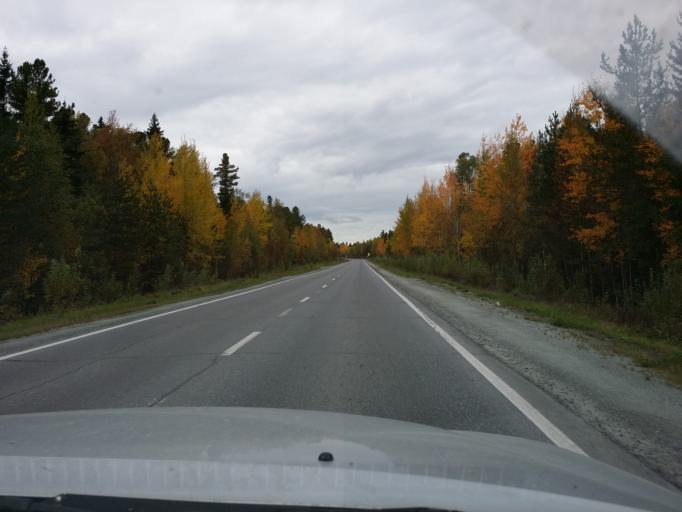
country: RU
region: Khanty-Mansiyskiy Avtonomnyy Okrug
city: Langepas
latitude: 61.2126
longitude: 75.3650
